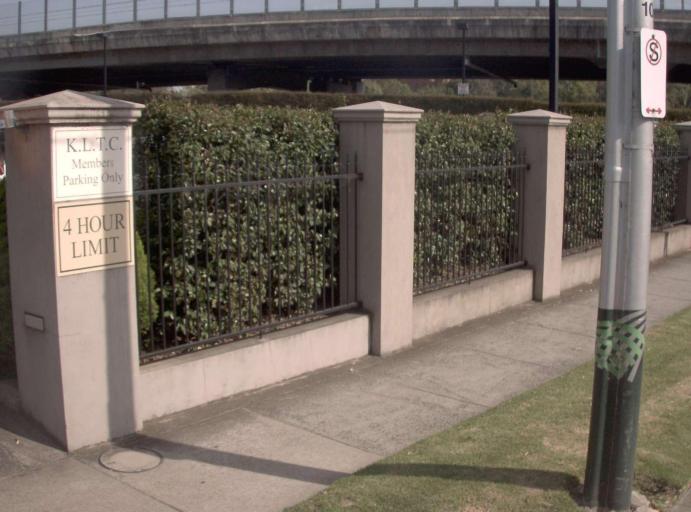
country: AU
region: Victoria
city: Glenferrie
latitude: -37.8379
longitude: 145.0325
